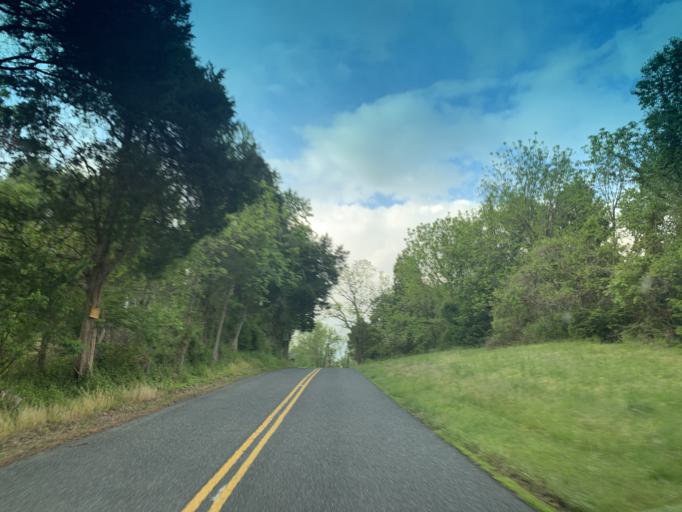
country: US
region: Pennsylvania
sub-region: York County
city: Susquehanna Trails
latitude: 39.6959
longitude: -76.2771
